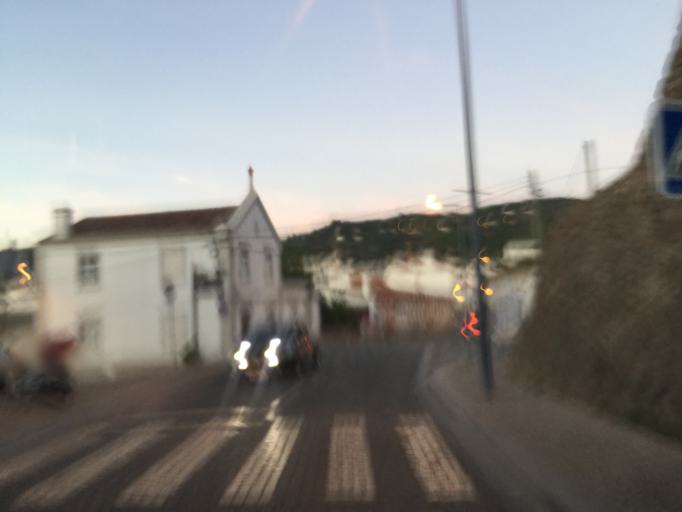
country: PT
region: Portalegre
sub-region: Portalegre
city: Portalegre
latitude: 39.2936
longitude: -7.4325
